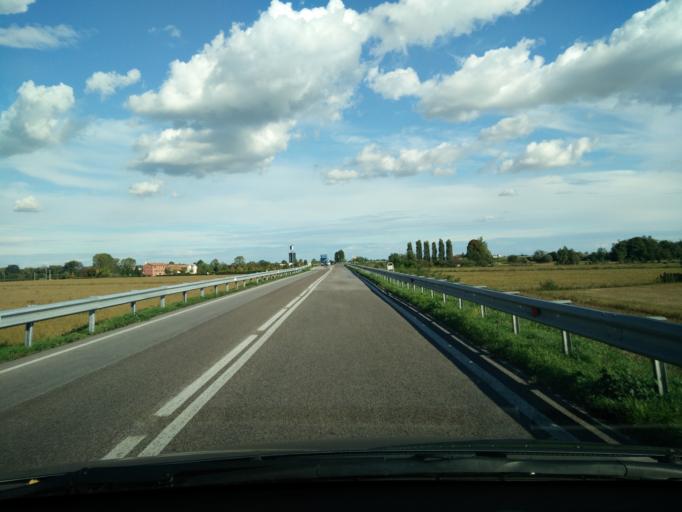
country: IT
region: Veneto
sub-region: Provincia di Treviso
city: Talponada
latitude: 45.6938
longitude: 12.4942
